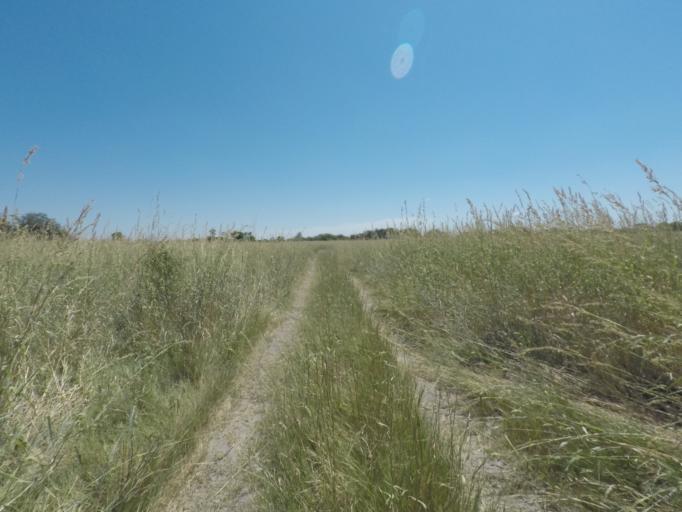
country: BW
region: North West
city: Maun
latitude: -19.4872
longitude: 23.5276
